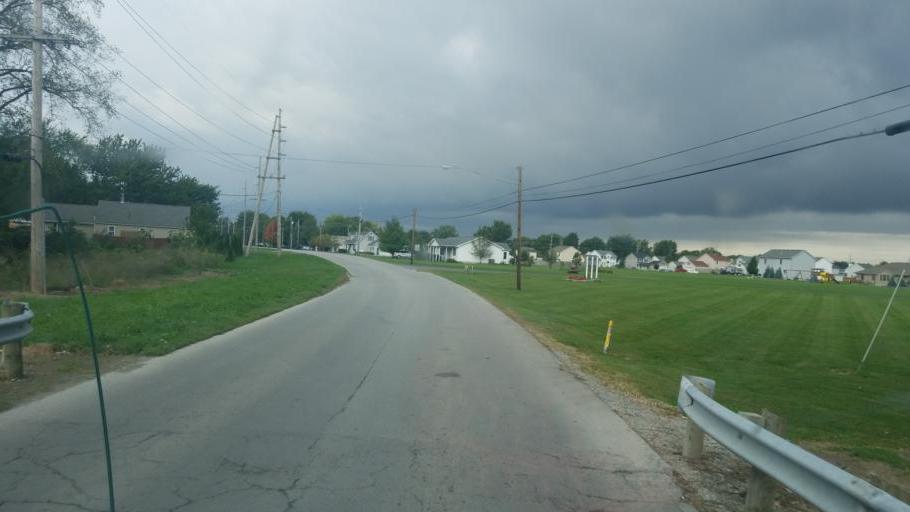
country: US
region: Ohio
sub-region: Wood County
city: North Baltimore
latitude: 41.1825
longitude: -83.6640
